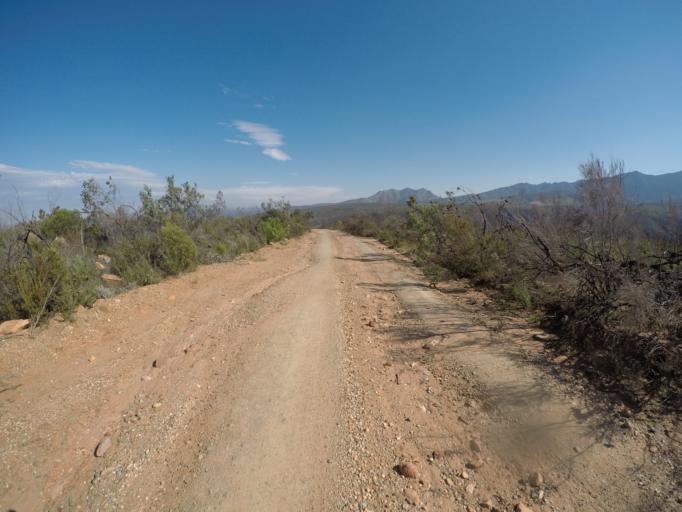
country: ZA
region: Eastern Cape
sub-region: Cacadu District Municipality
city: Kareedouw
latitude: -33.6364
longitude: 24.4558
